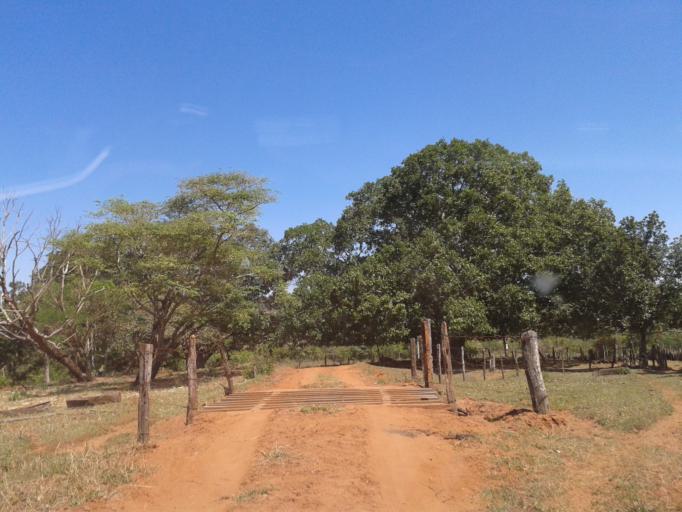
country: BR
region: Minas Gerais
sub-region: Ituiutaba
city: Ituiutaba
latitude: -19.1110
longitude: -49.2751
